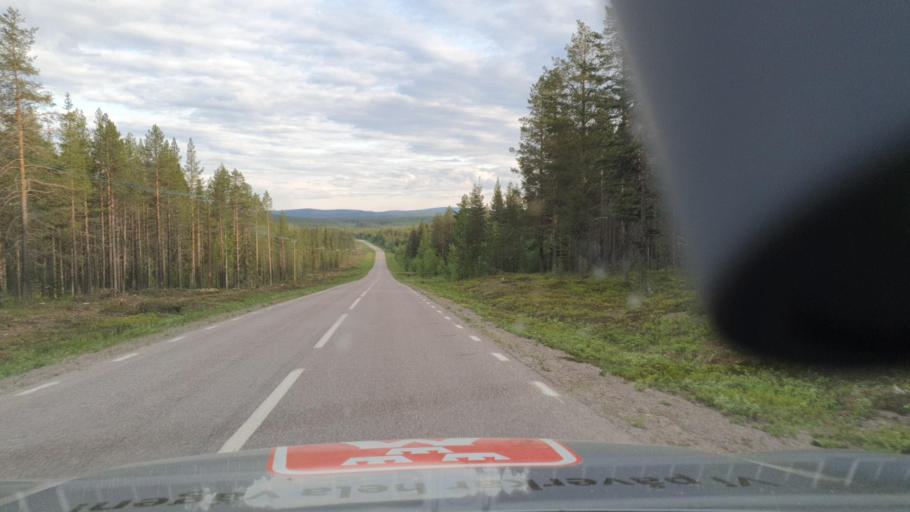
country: SE
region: Norrbotten
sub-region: Gallivare Kommun
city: Gaellivare
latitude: 66.9568
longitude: 21.2347
